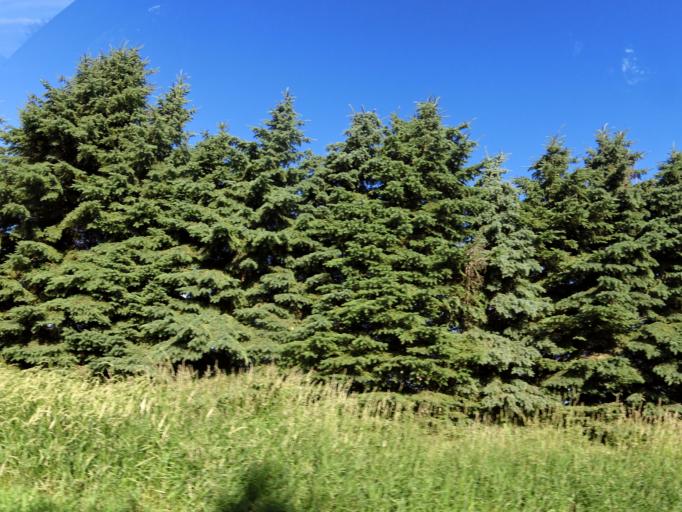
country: US
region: Minnesota
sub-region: Dakota County
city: Hastings
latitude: 44.8175
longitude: -92.8629
